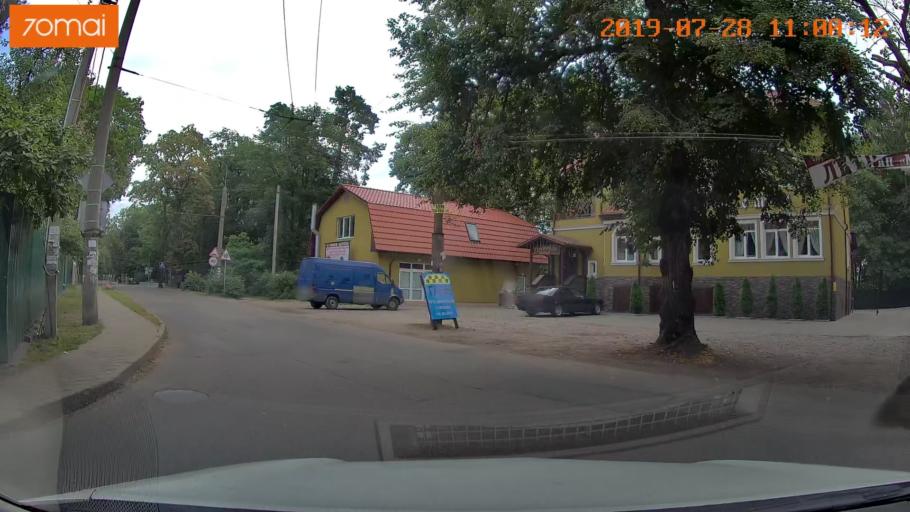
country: RU
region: Kaliningrad
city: Vzmorye
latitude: 54.7264
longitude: 20.3603
